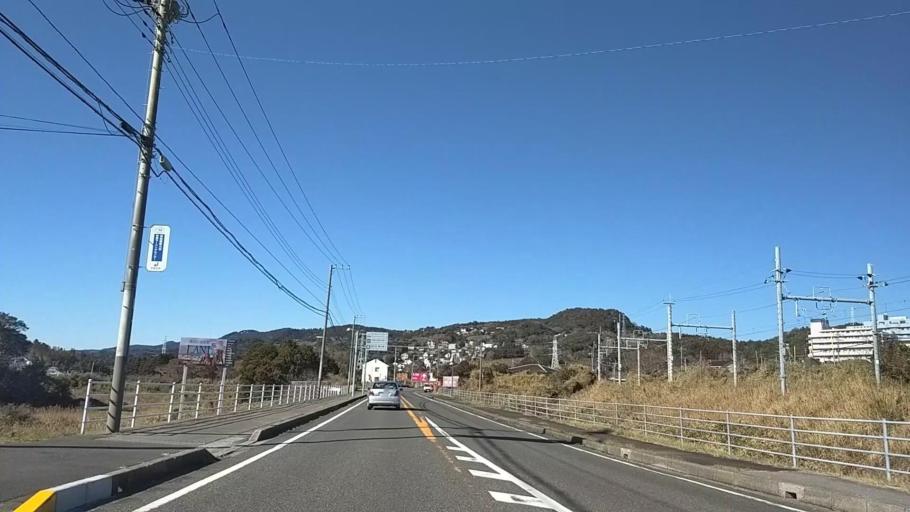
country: JP
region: Chiba
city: Kawaguchi
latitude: 35.0869
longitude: 140.0925
